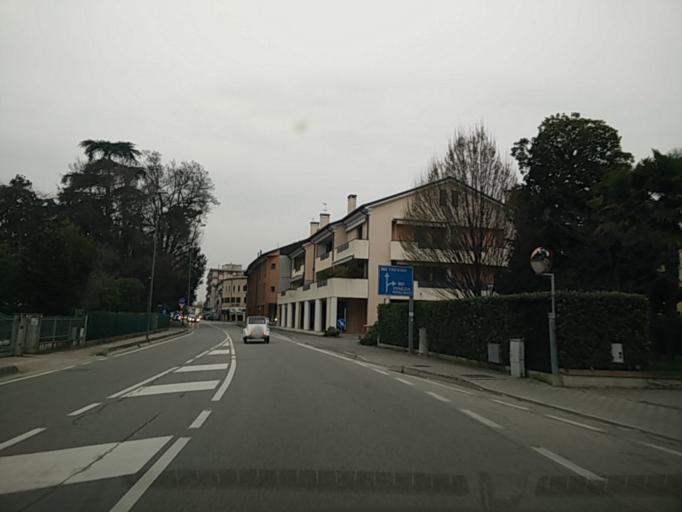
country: IT
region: Veneto
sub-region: Provincia di Venezia
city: Scorze
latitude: 45.5688
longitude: 12.1084
